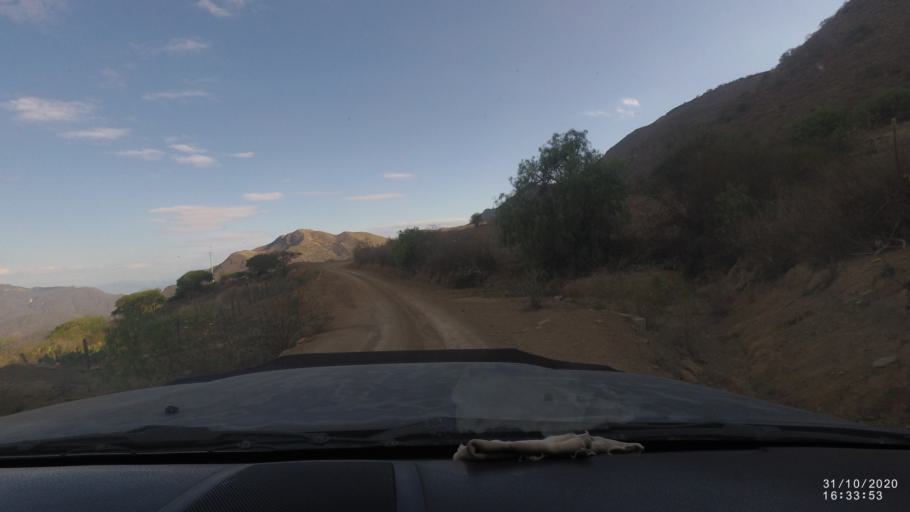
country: BO
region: Chuquisaca
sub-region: Provincia Zudanez
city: Mojocoya
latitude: -18.4454
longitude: -64.5844
